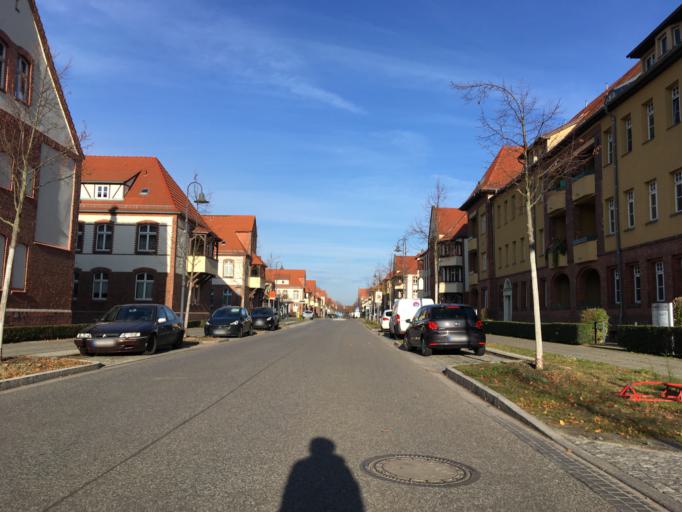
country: DE
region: Brandenburg
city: Wildau
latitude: 52.3179
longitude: 13.6341
